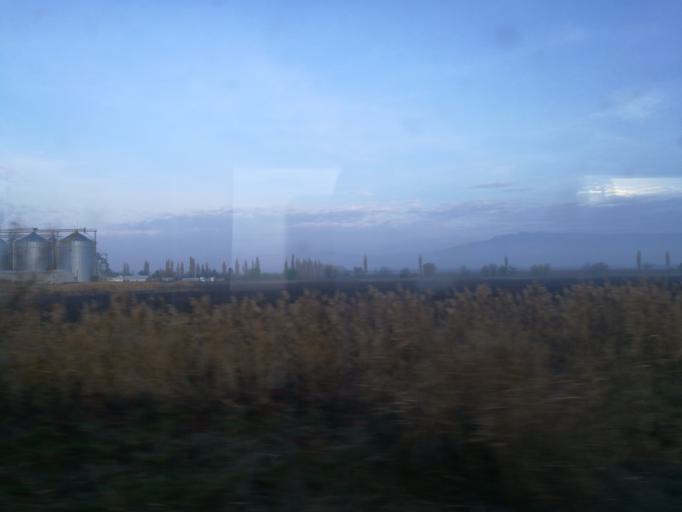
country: RO
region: Buzau
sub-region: Comuna Breaza
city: Greceanca
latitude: 45.0428
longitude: 26.5527
